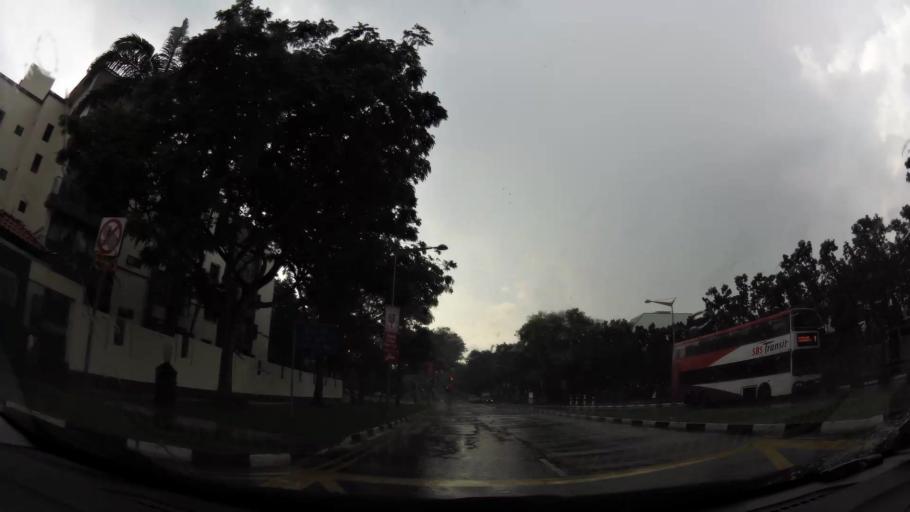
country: SG
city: Singapore
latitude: 1.3329
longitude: 103.9474
